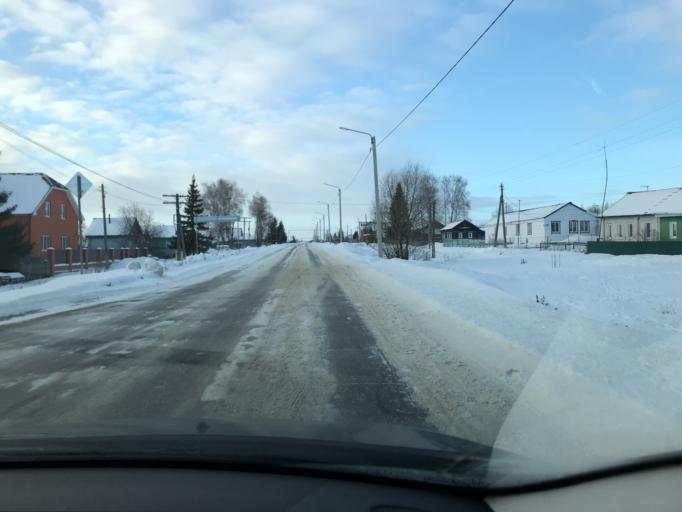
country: RU
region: Ulyanovsk
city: Undory
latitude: 54.6033
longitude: 48.4134
